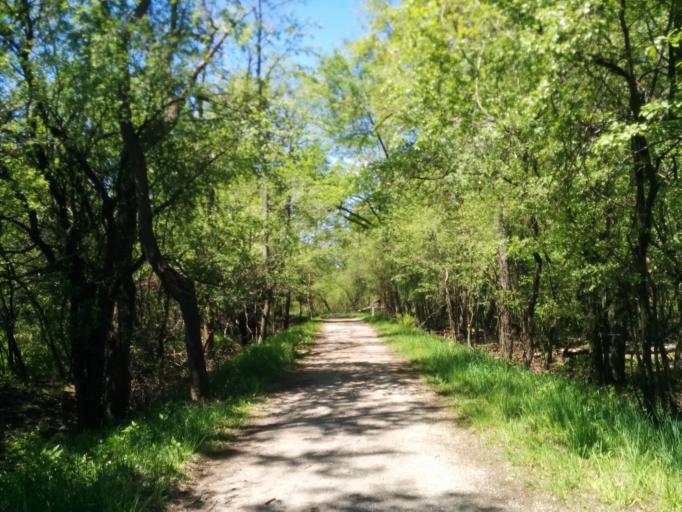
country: US
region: Illinois
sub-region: Cook County
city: Schiller Park
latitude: 41.9808
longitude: -87.8549
